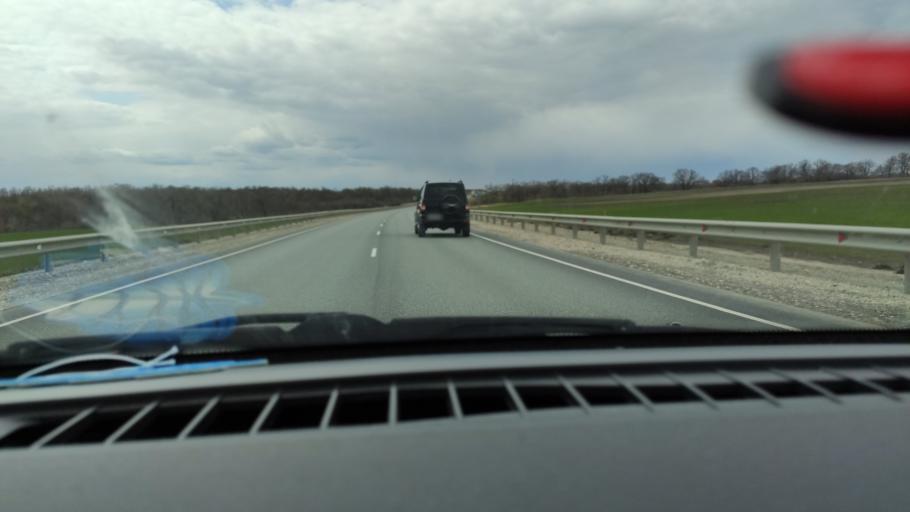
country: RU
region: Saratov
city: Yelshanka
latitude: 51.8310
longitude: 46.4464
